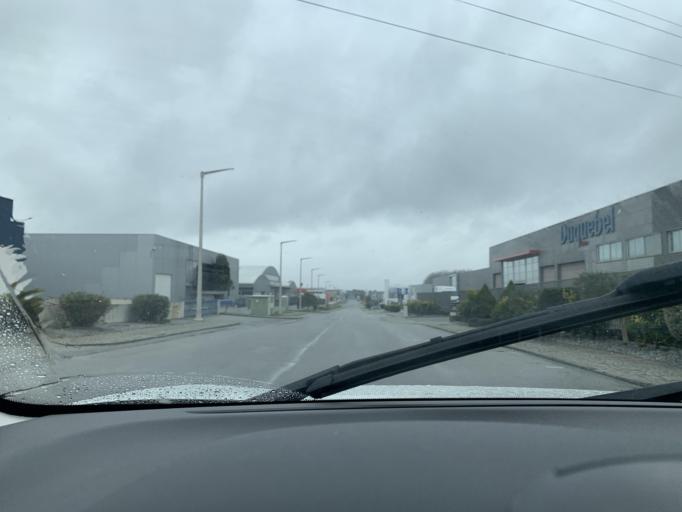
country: PT
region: Viseu
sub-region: Viseu
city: Rio de Loba
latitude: 40.6301
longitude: -7.8678
